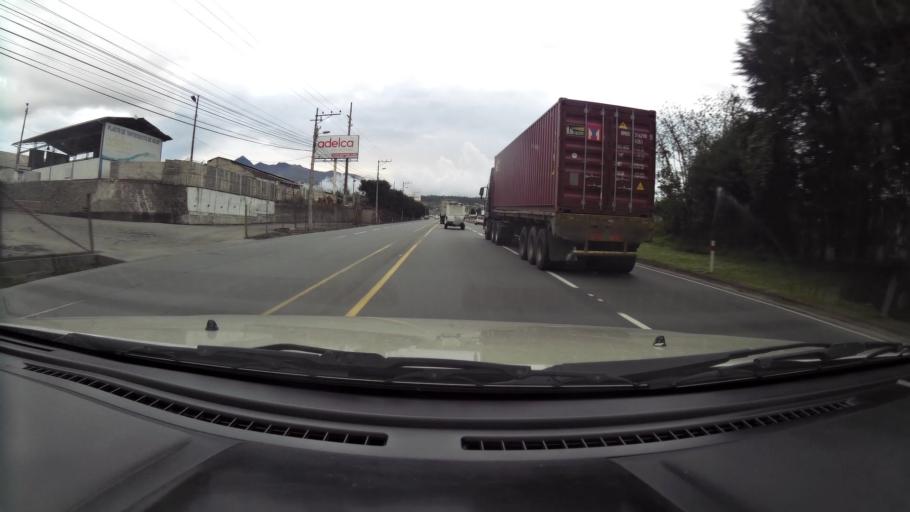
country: EC
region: Pichincha
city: Machachi
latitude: -0.4440
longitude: -78.6296
